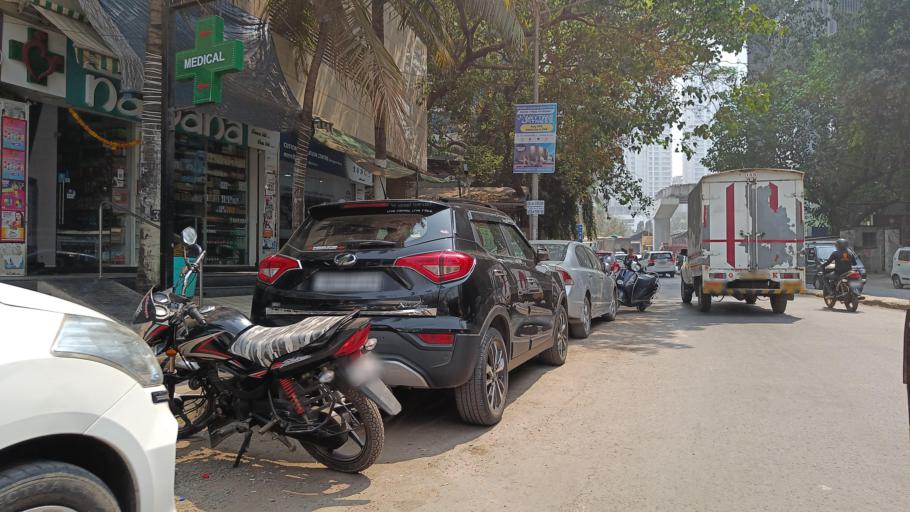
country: IN
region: Maharashtra
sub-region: Mumbai Suburban
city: Powai
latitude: 19.1524
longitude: 72.8435
